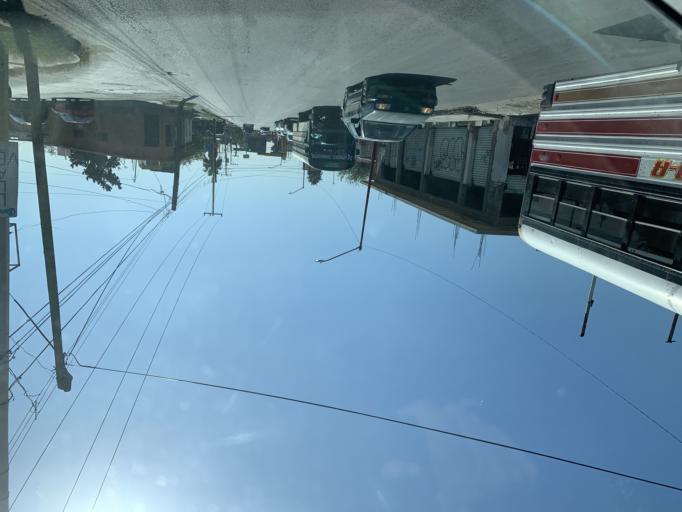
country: MX
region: Chihuahua
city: Ciudad Juarez
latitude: 31.7203
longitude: -106.4642
